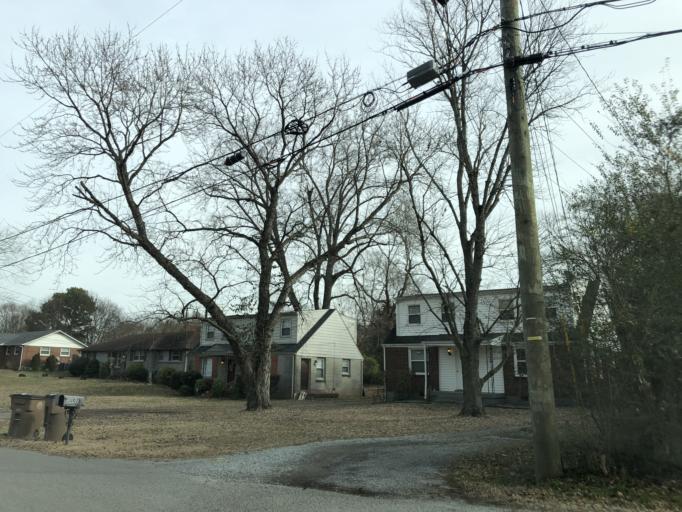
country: US
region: Tennessee
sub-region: Davidson County
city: Nashville
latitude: 36.2107
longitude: -86.7218
